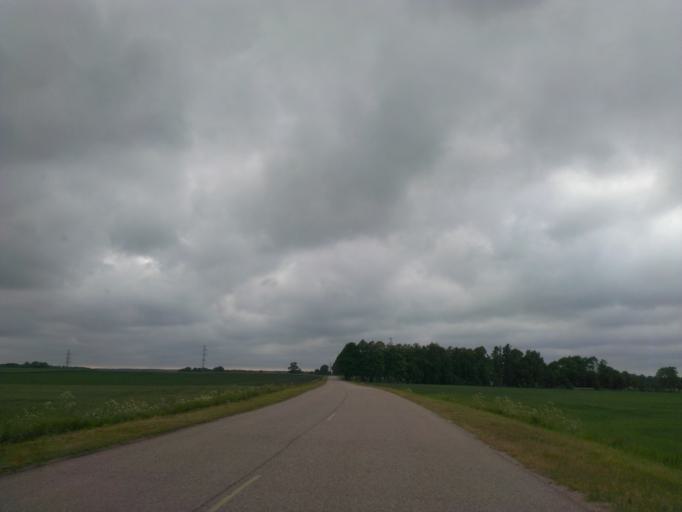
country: LV
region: Aizpute
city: Aizpute
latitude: 56.7211
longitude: 21.4442
